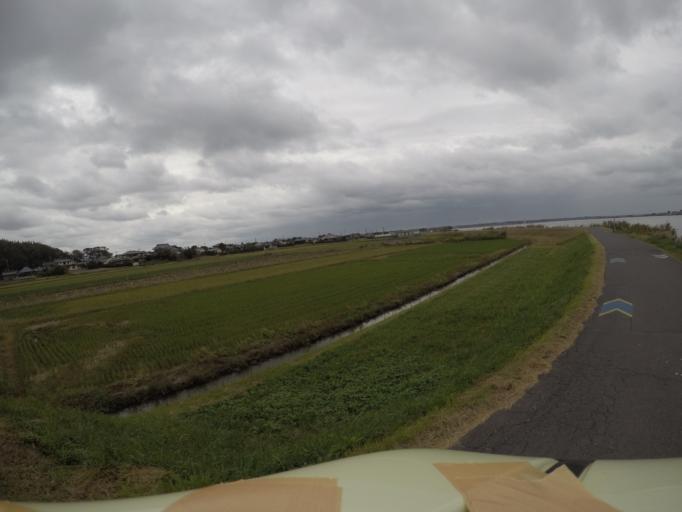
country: JP
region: Ibaraki
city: Ishioka
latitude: 36.1007
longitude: 140.3738
